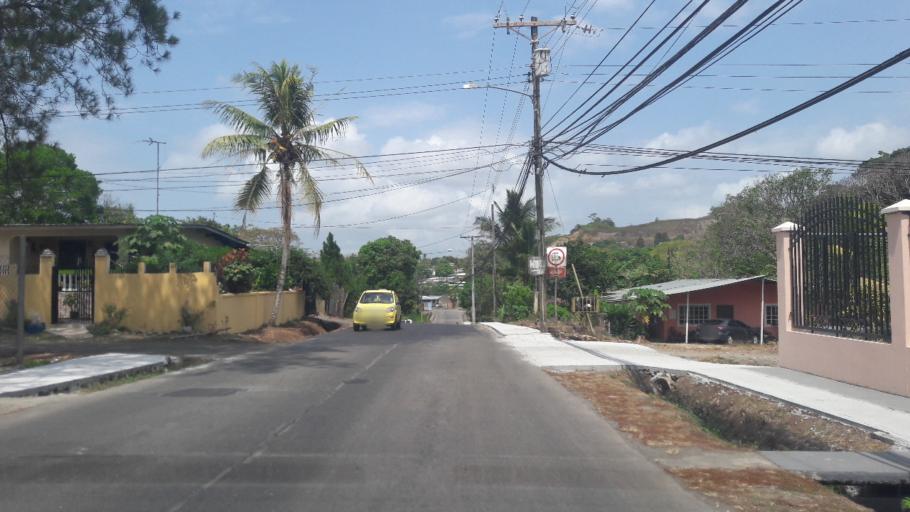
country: PA
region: Panama
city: Alcalde Diaz
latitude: 9.1367
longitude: -79.5527
